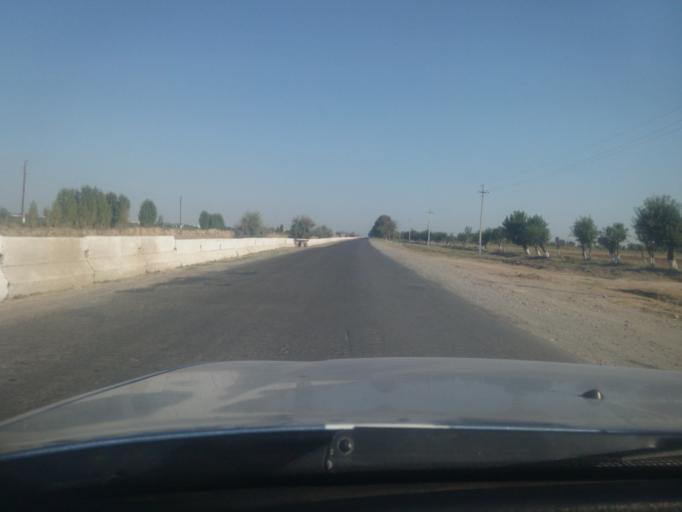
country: UZ
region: Sirdaryo
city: Guliston
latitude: 40.4987
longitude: 68.7990
